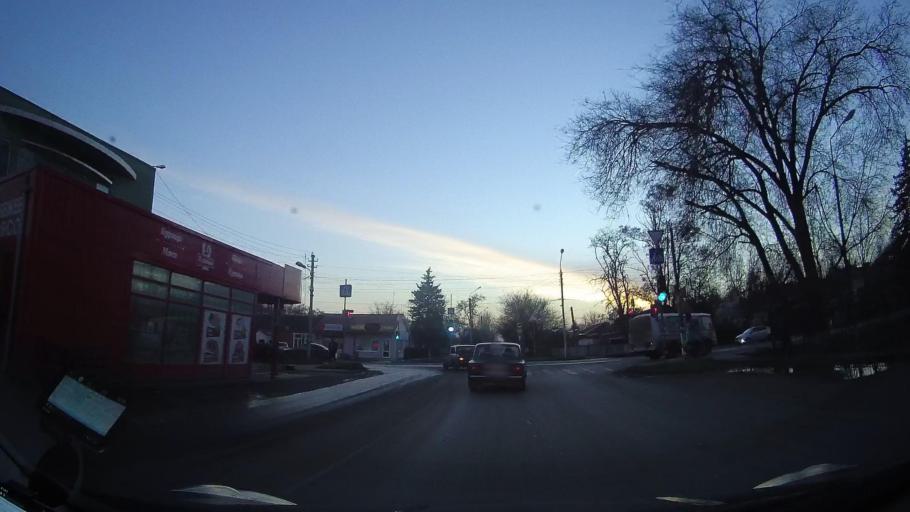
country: RU
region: Rostov
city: Zernograd
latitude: 46.8521
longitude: 40.3103
